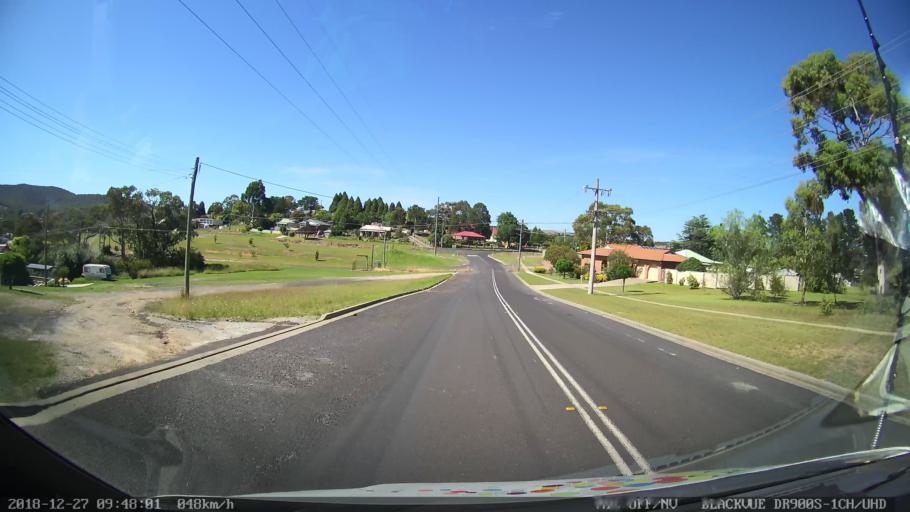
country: AU
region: New South Wales
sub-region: Lithgow
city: Portland
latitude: -33.3510
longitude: 149.9892
